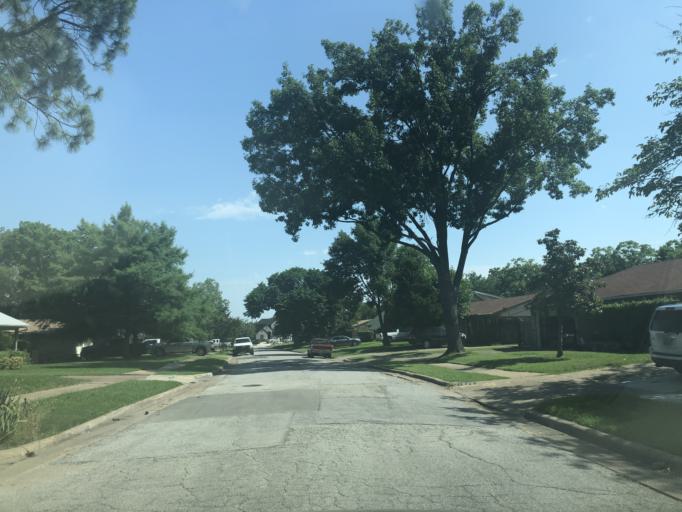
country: US
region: Texas
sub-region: Dallas County
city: Grand Prairie
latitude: 32.7227
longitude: -97.0034
